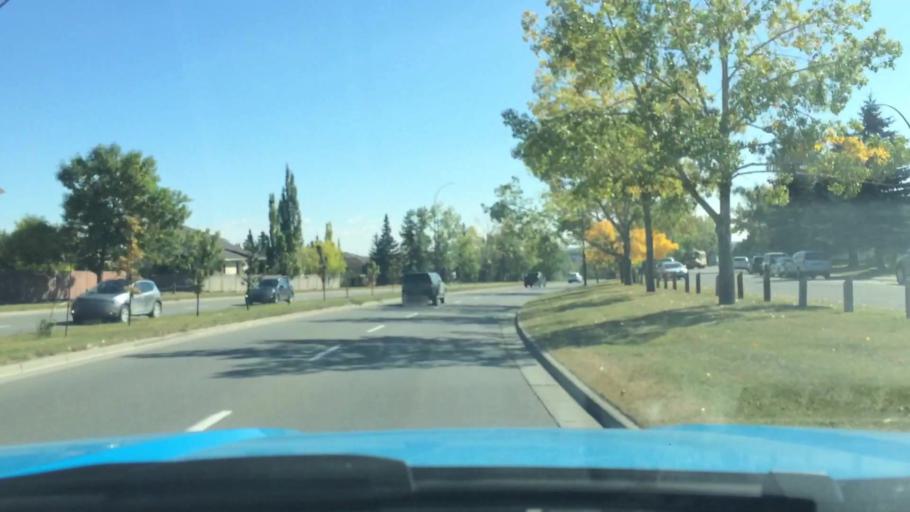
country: CA
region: Alberta
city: Calgary
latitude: 50.9139
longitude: -114.0804
